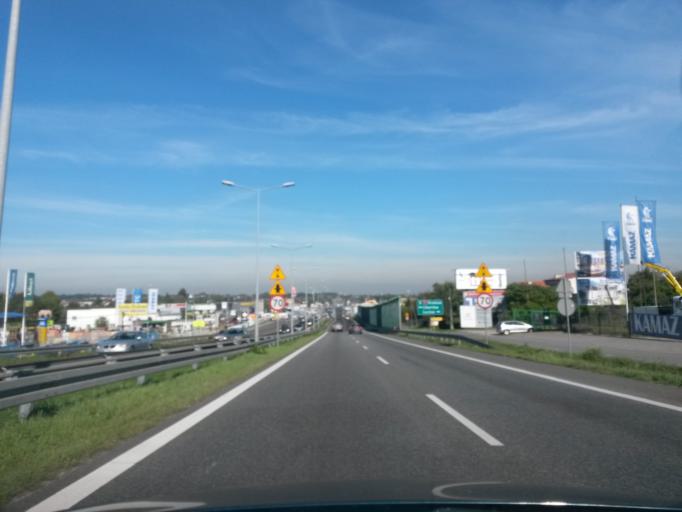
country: PL
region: Lesser Poland Voivodeship
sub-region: Powiat krakowski
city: Libertow
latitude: 49.9761
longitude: 19.9086
